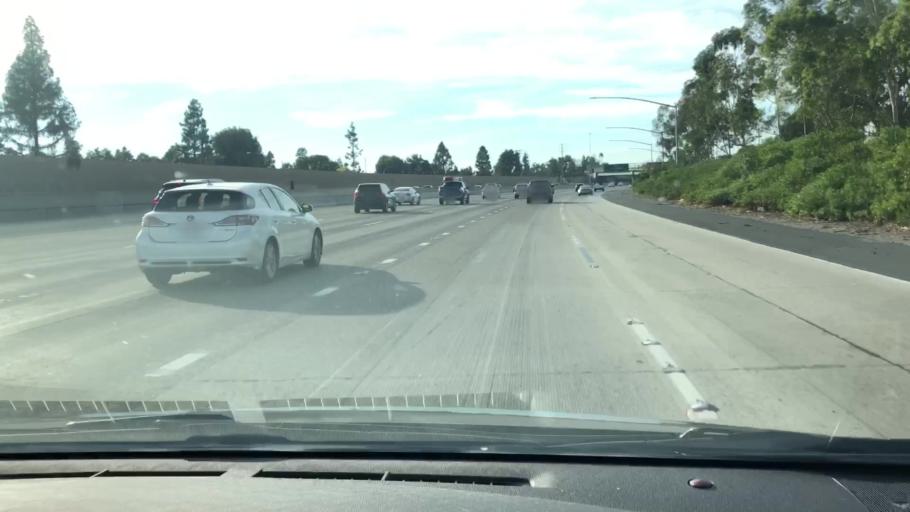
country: US
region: California
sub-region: Orange County
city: Placentia
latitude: 33.8466
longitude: -117.8663
